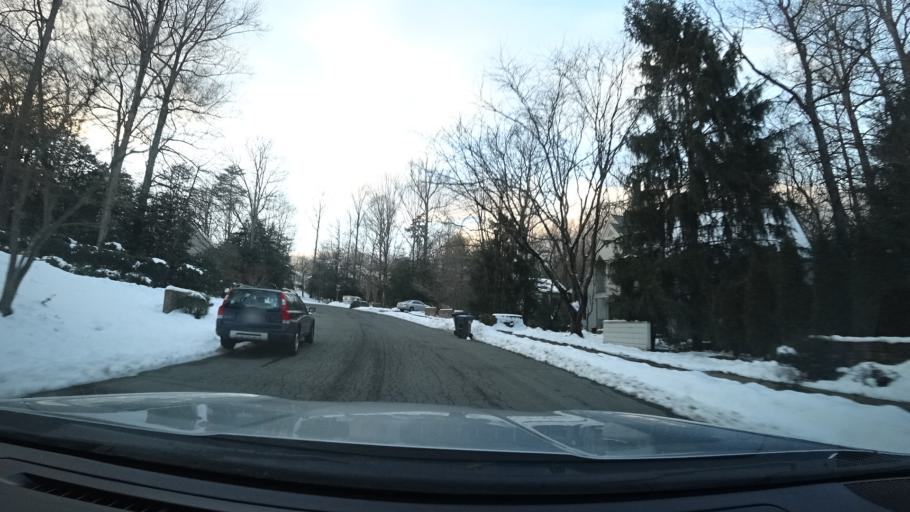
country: US
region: Virginia
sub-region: Fairfax County
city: Reston
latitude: 38.9764
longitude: -77.3439
